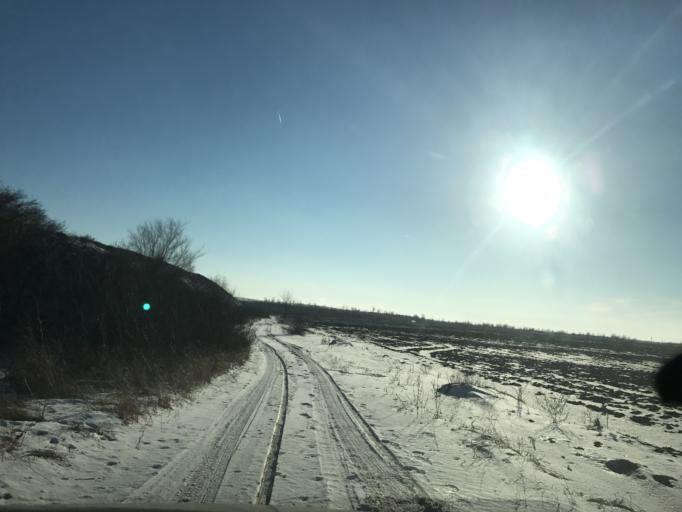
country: RU
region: Rostov
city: Staraya Stanitsa
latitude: 48.2394
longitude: 40.3944
